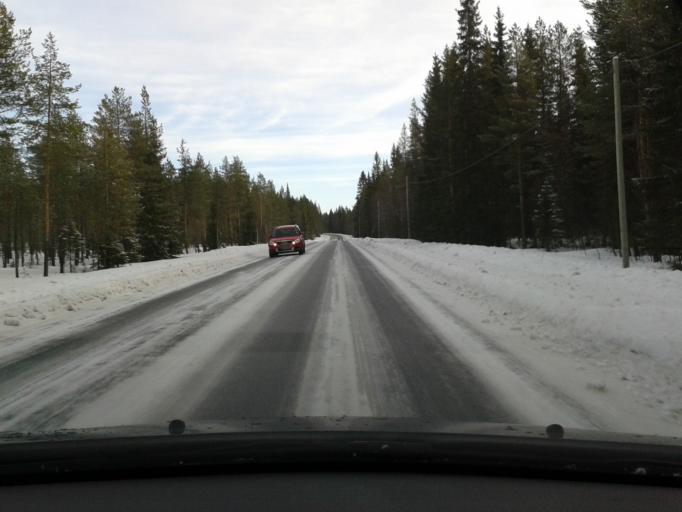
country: SE
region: Vaesterbotten
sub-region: Vilhelmina Kommun
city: Vilhelmina
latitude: 64.6477
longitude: 16.5199
